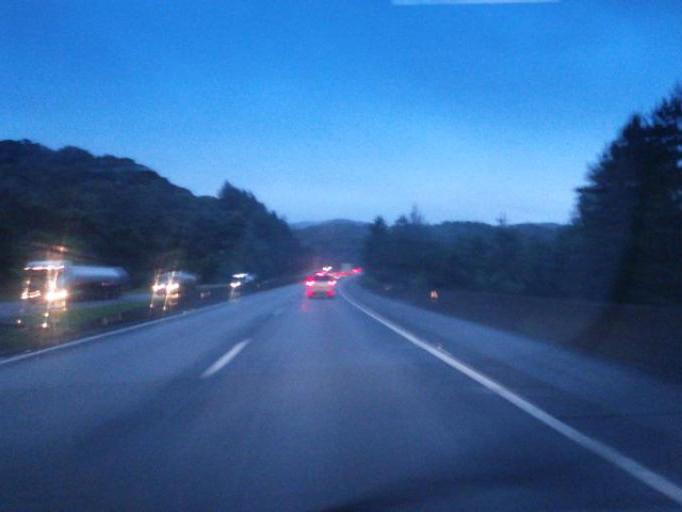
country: BR
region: Sao Paulo
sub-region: Juquitiba
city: Juquitiba
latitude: -23.9490
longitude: -47.1003
